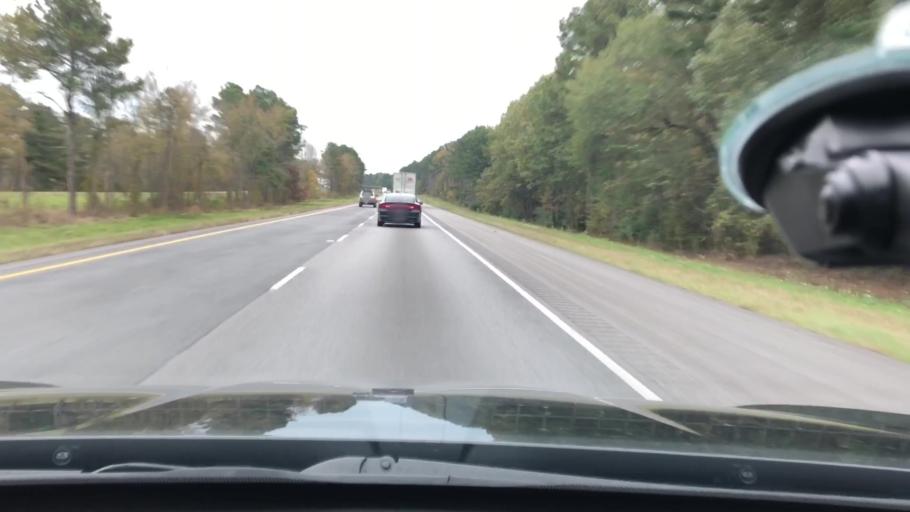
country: US
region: Arkansas
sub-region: Hempstead County
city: Hope
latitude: 33.6279
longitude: -93.7381
